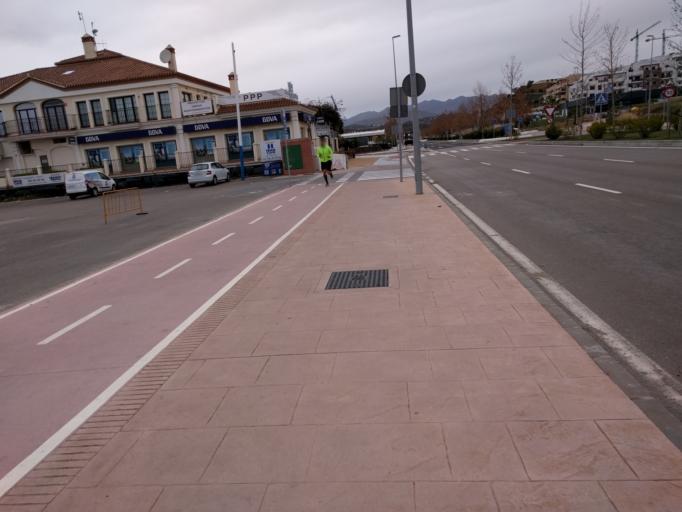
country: ES
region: Andalusia
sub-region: Provincia de Malaga
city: Fuengirola
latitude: 36.5059
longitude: -4.6818
